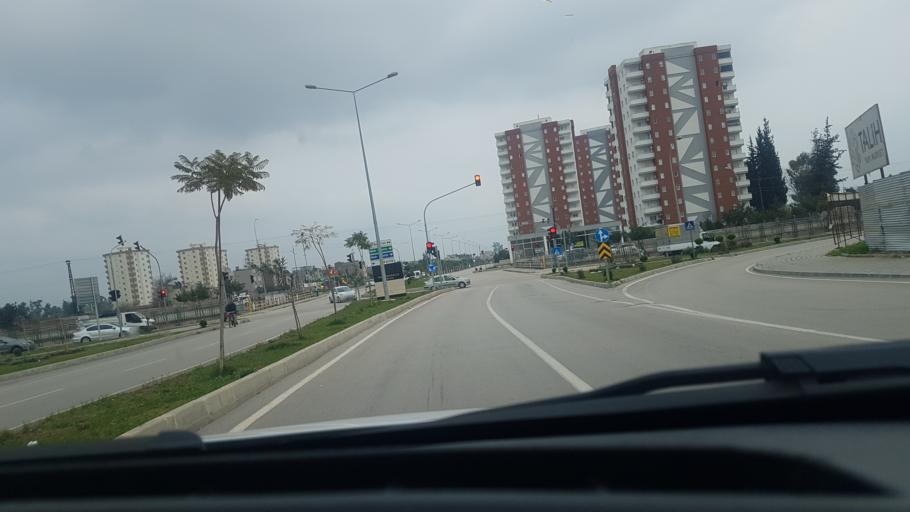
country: TR
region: Adana
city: Seyhan
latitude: 37.0081
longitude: 35.2574
